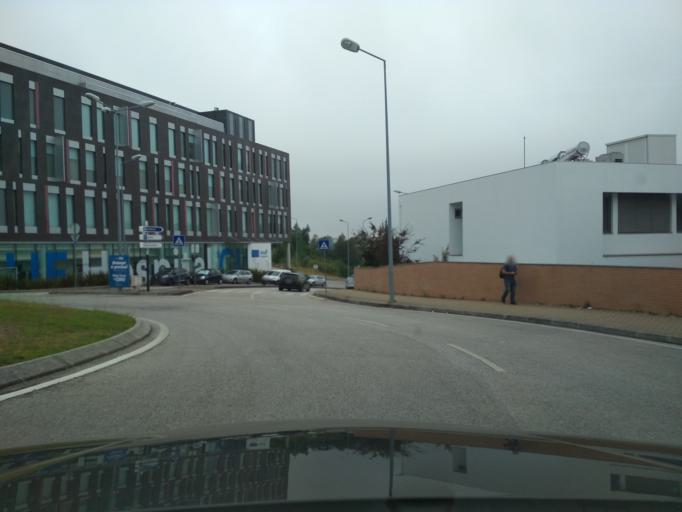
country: PT
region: Coimbra
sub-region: Coimbra
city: Coimbra
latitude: 40.2229
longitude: -8.4149
